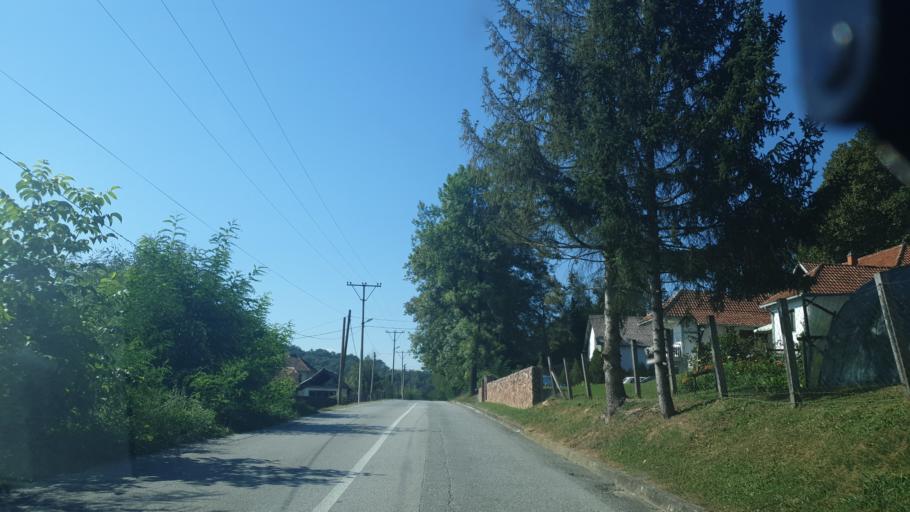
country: RS
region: Central Serbia
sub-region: Kolubarski Okrug
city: Lajkovac
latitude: 44.3248
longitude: 20.1945
